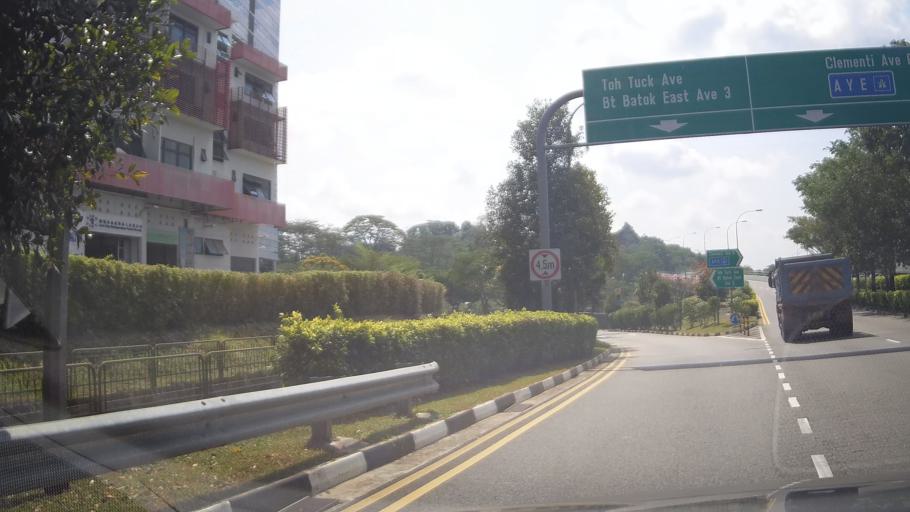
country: SG
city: Singapore
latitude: 1.3365
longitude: 103.7584
